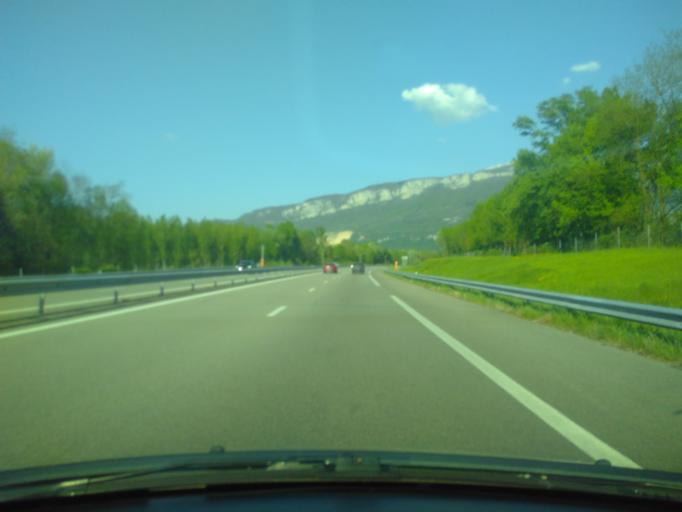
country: FR
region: Rhone-Alpes
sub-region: Departement de l'Isere
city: Veurey-Voroize
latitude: 45.3013
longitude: 5.5868
